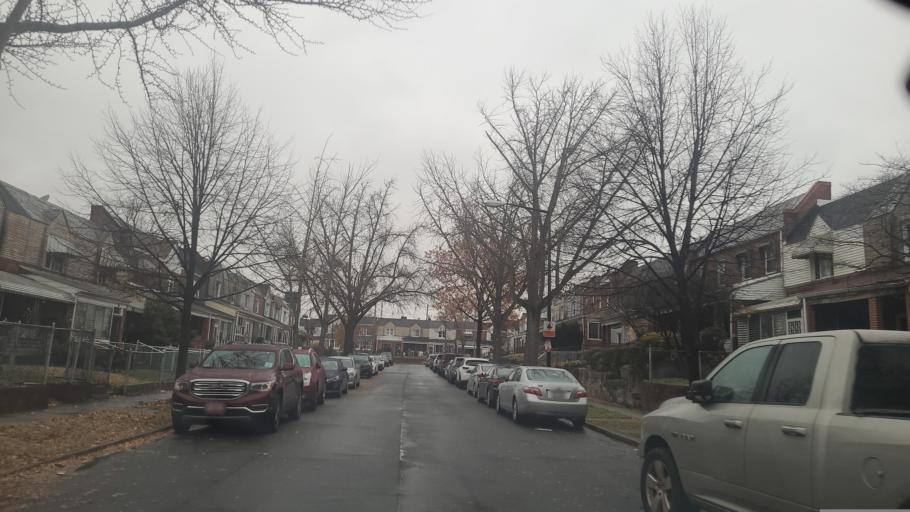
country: US
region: Maryland
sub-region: Prince George's County
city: Colmar Manor
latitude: 38.8972
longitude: -76.9555
